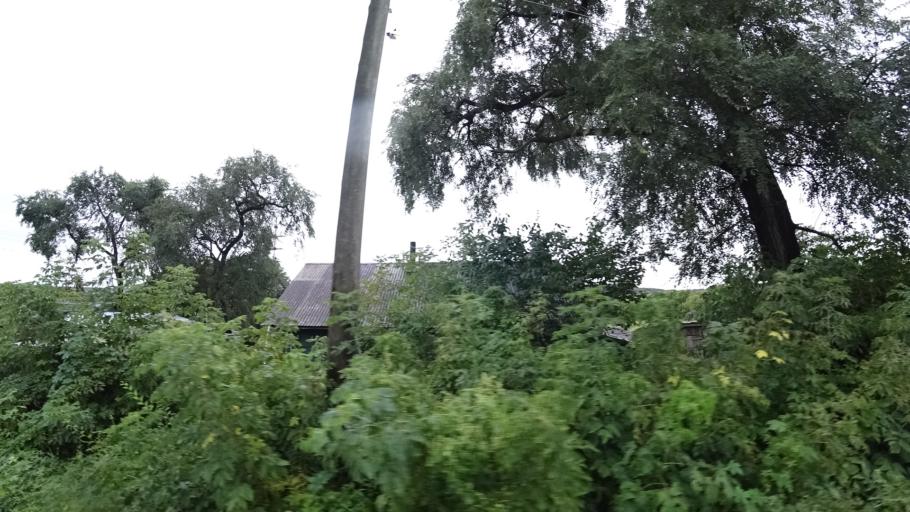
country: RU
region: Primorskiy
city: Monastyrishche
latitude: 44.2630
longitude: 132.4048
